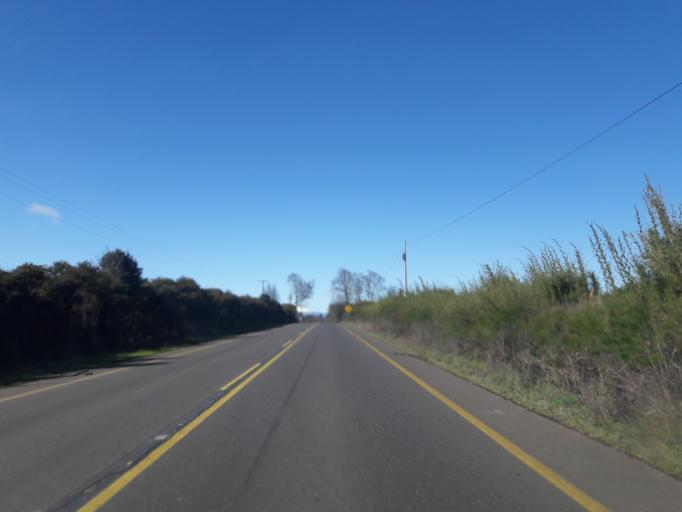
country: CL
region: Araucania
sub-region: Provincia de Malleco
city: Victoria
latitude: -38.2610
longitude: -72.2497
